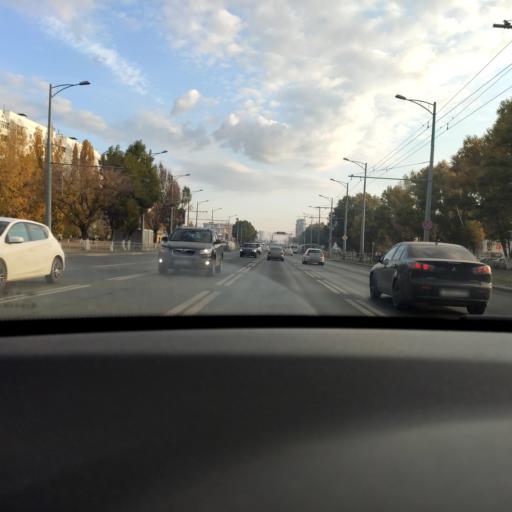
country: RU
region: Samara
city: Samara
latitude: 53.2457
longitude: 50.2138
